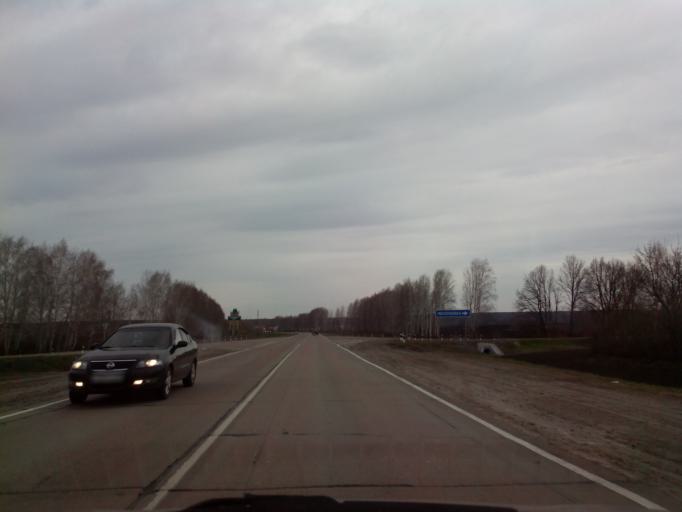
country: RU
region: Tambov
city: Znamenka
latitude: 52.5129
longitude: 41.3644
